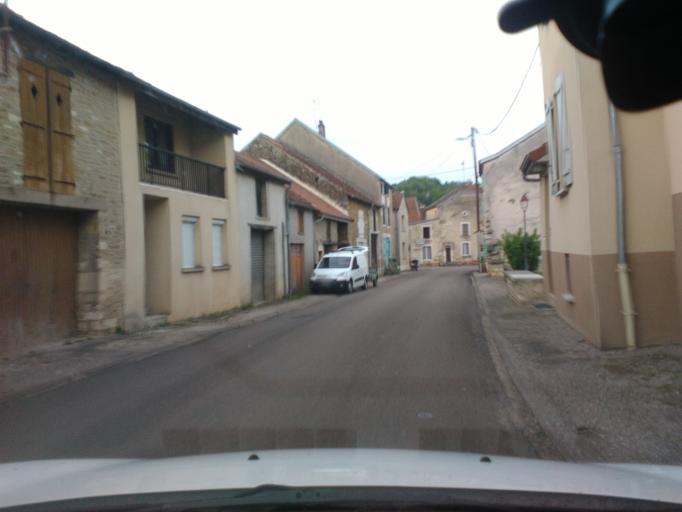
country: FR
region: Champagne-Ardenne
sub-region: Departement de la Haute-Marne
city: Doulaincourt-Saucourt
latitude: 48.2433
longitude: 5.2937
